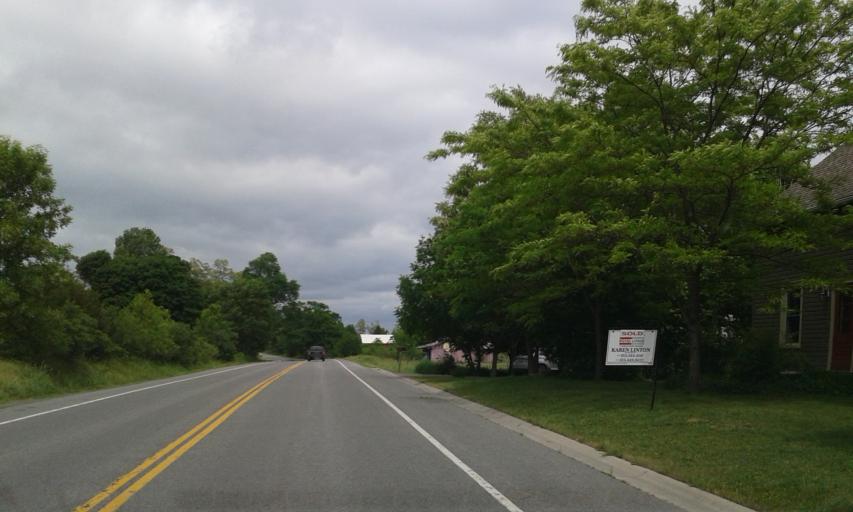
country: CA
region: Ontario
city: Deseronto
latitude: 44.0838
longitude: -76.9614
